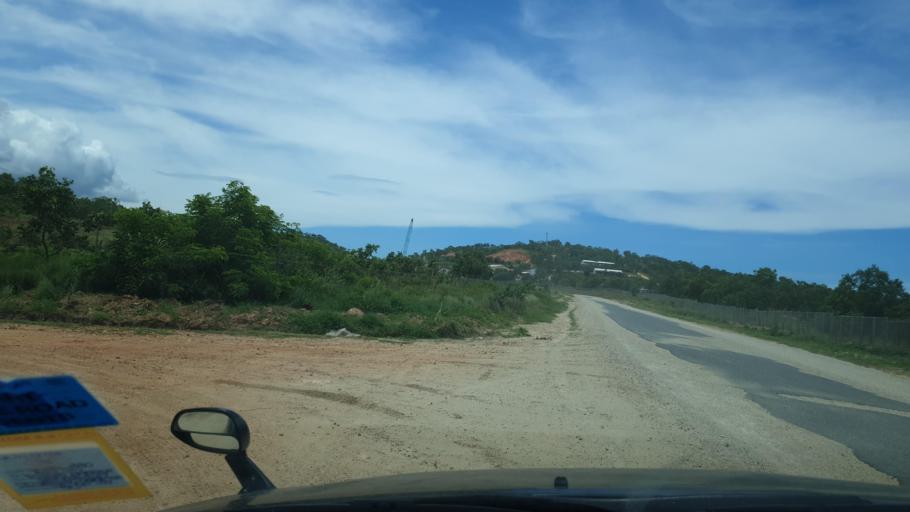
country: PG
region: National Capital
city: Port Moresby
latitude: -9.4459
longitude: 147.0798
